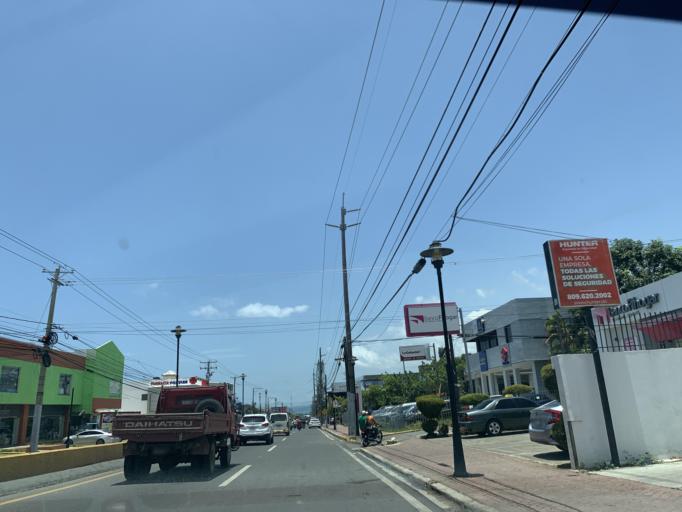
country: DO
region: Puerto Plata
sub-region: Puerto Plata
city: Puerto Plata
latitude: 19.7846
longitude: -70.6822
